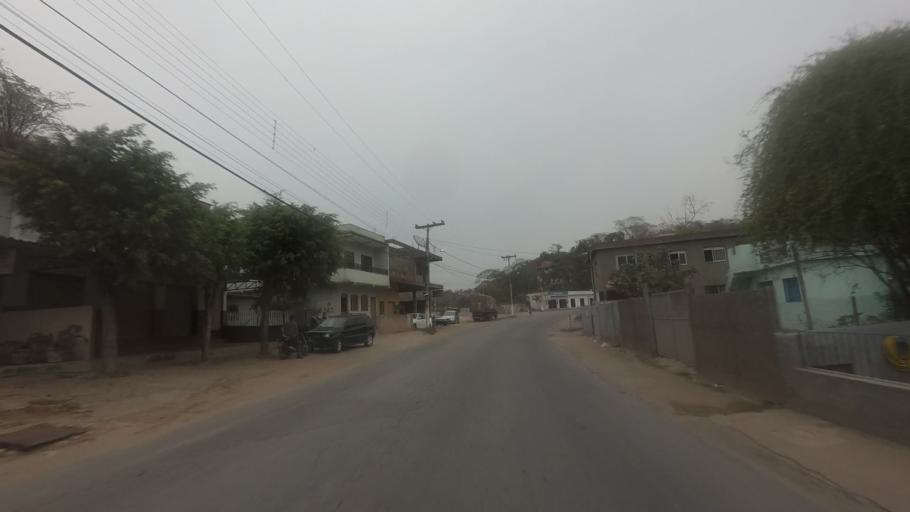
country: BR
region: Minas Gerais
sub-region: Recreio
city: Recreio
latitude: -21.6578
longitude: -42.3508
